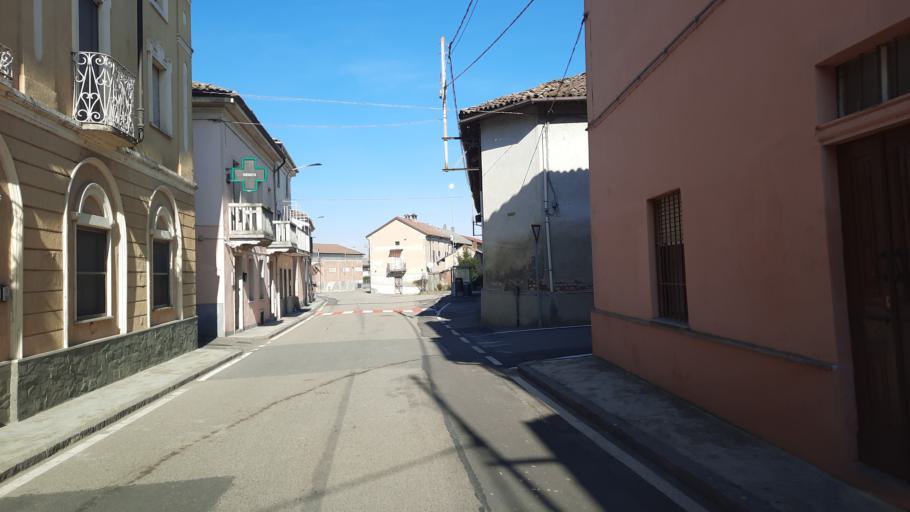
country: IT
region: Piedmont
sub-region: Provincia di Vercelli
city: Rive
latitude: 45.2134
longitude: 8.4181
